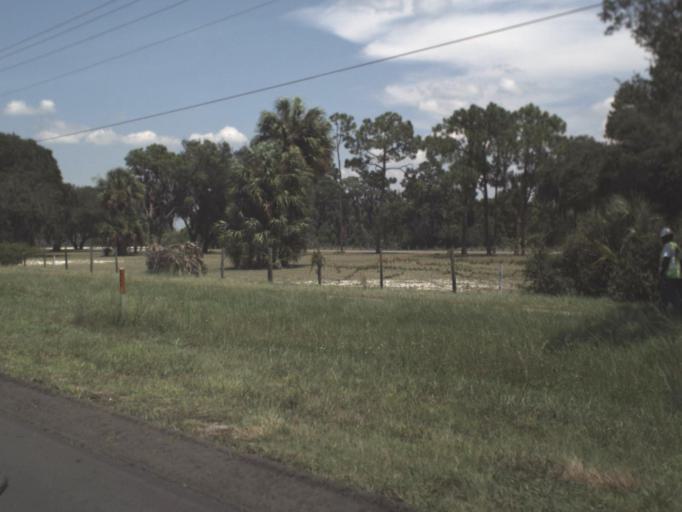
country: US
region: Florida
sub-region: Hillsborough County
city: Ruskin
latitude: 27.6939
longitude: -82.4624
